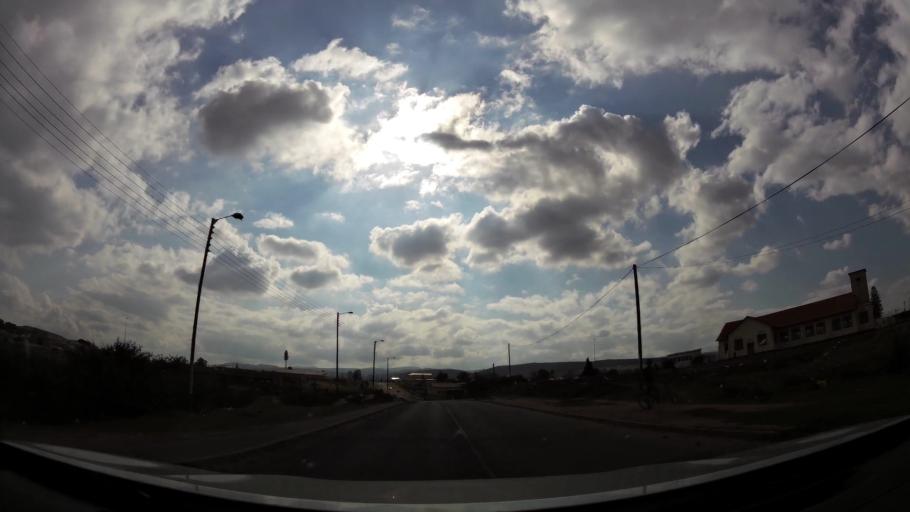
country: ZA
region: Eastern Cape
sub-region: Nelson Mandela Bay Metropolitan Municipality
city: Uitenhage
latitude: -33.7479
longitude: 25.3906
